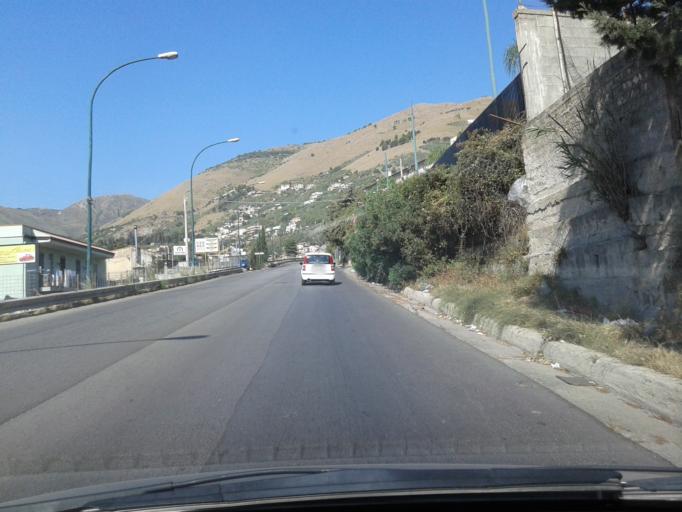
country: IT
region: Sicily
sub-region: Palermo
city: Monreale
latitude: 38.0743
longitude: 13.2852
